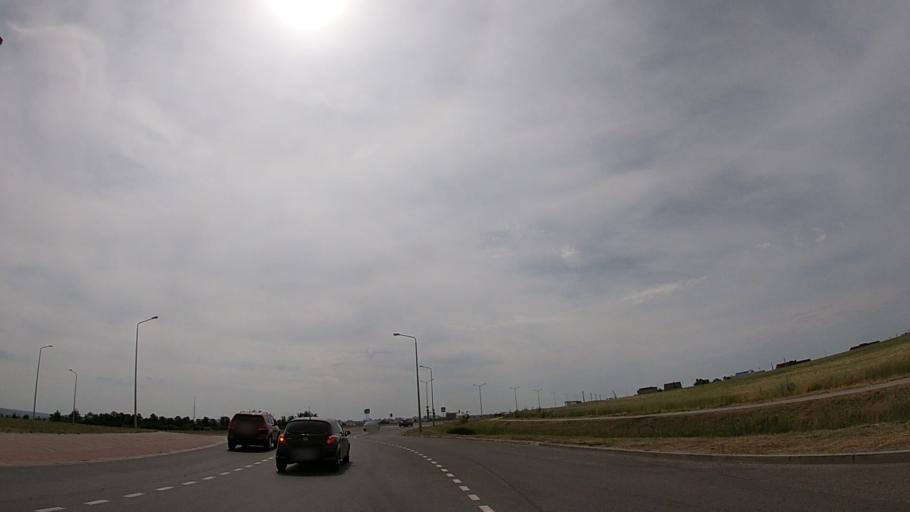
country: RU
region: Belgorod
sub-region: Belgorodskiy Rayon
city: Belgorod
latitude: 50.5932
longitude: 36.5303
